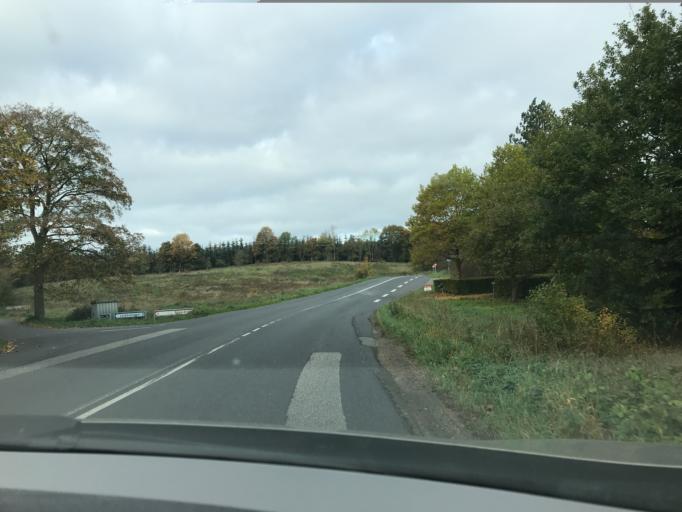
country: DK
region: South Denmark
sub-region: Kolding Kommune
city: Kolding
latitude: 55.5289
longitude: 9.4243
